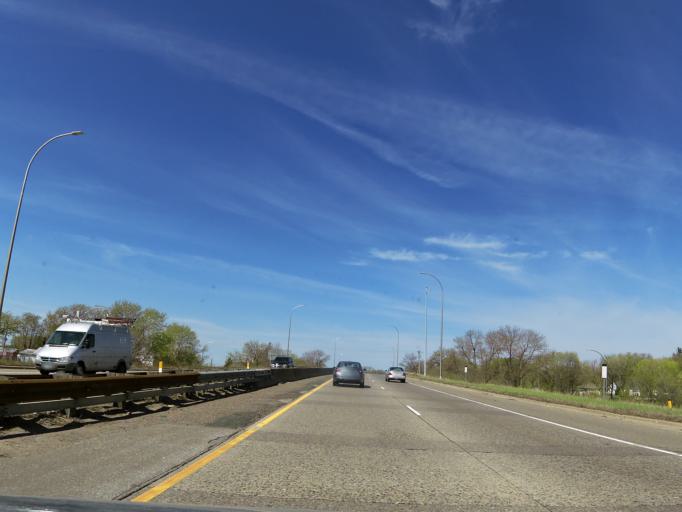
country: US
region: Minnesota
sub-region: Hennepin County
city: Richfield
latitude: 44.8975
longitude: -93.2301
